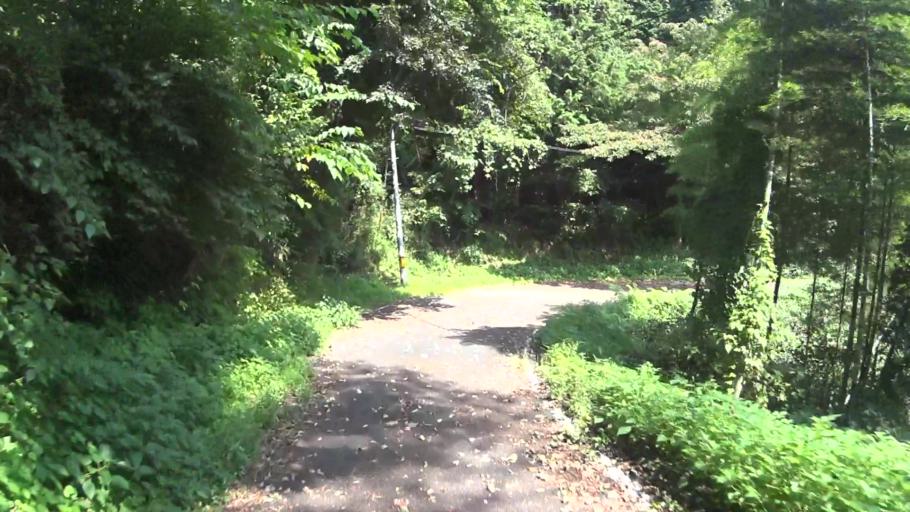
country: JP
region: Kyoto
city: Miyazu
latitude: 35.6563
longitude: 135.2398
